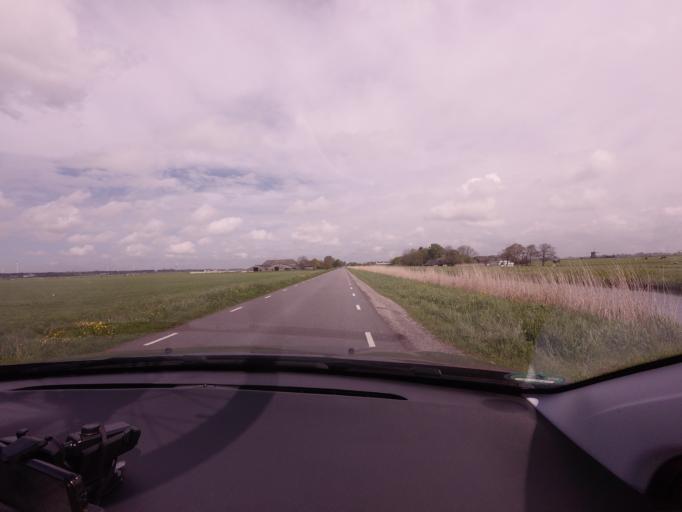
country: NL
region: North Holland
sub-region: Gemeente Alkmaar
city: Alkmaar
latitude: 52.5757
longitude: 4.7744
